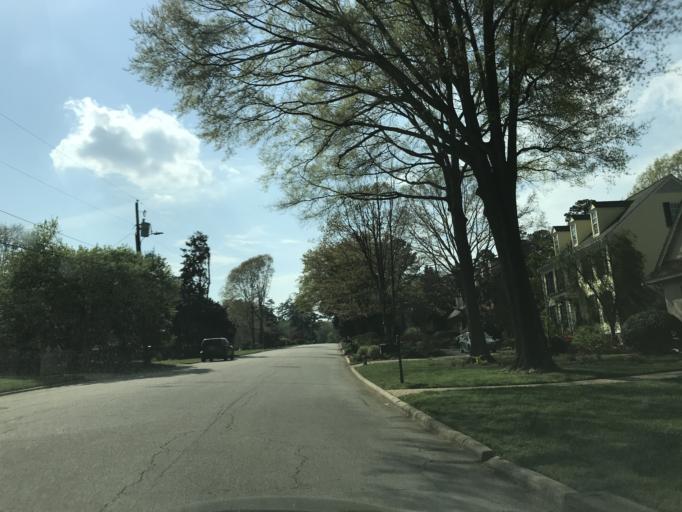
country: US
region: North Carolina
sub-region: Wake County
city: West Raleigh
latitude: 35.8056
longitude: -78.6820
